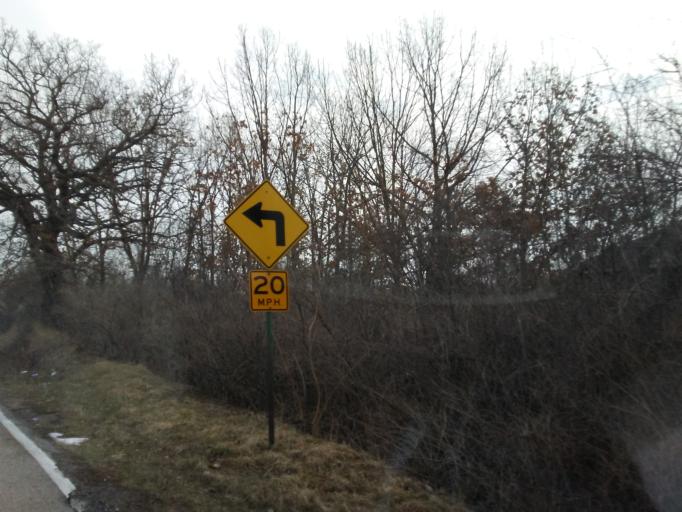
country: US
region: Wisconsin
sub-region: Dane County
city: Middleton
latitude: 43.1105
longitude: -89.4927
